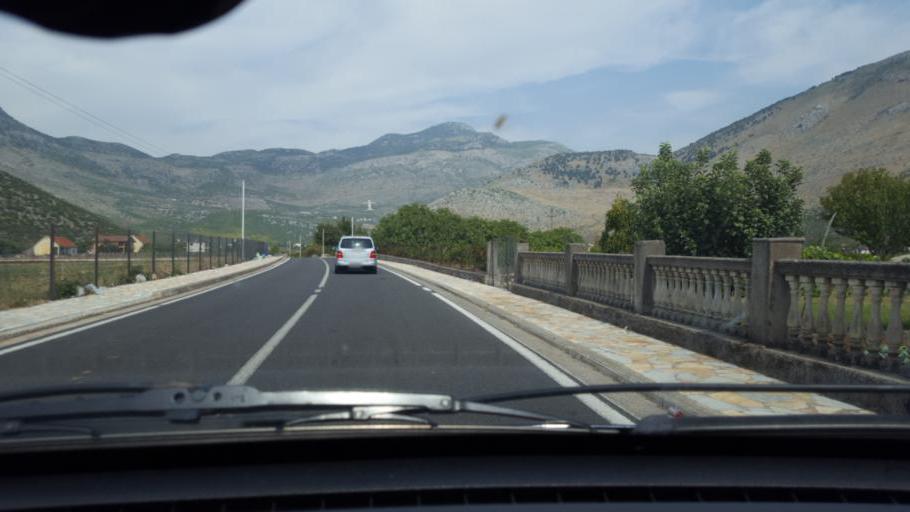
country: AL
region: Shkoder
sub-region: Rrethi i Malesia e Madhe
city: Hot
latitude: 42.3463
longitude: 19.4400
